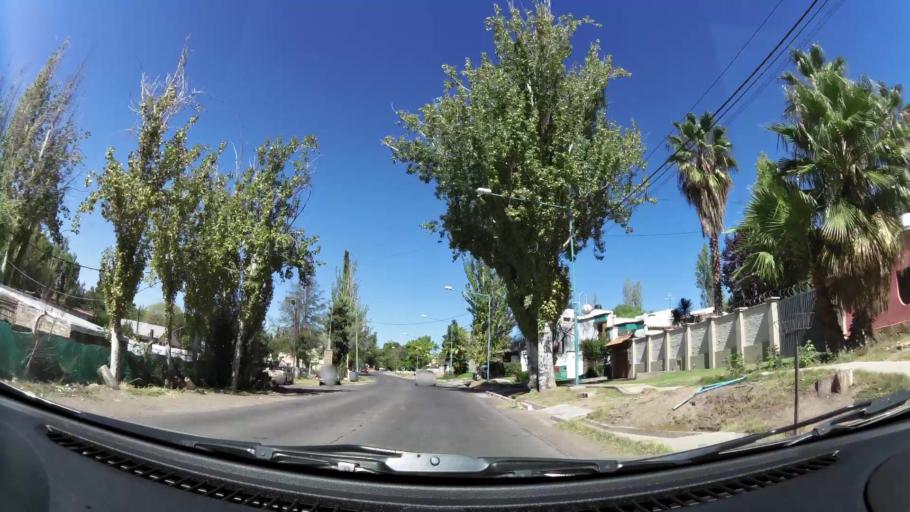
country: AR
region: Mendoza
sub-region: Departamento de Godoy Cruz
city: Godoy Cruz
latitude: -32.9569
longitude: -68.8531
